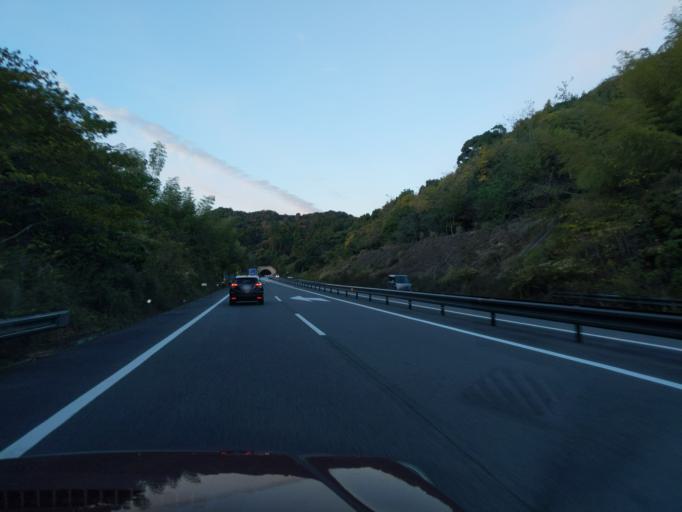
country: JP
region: Tokushima
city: Anan
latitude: 33.7735
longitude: 134.5798
